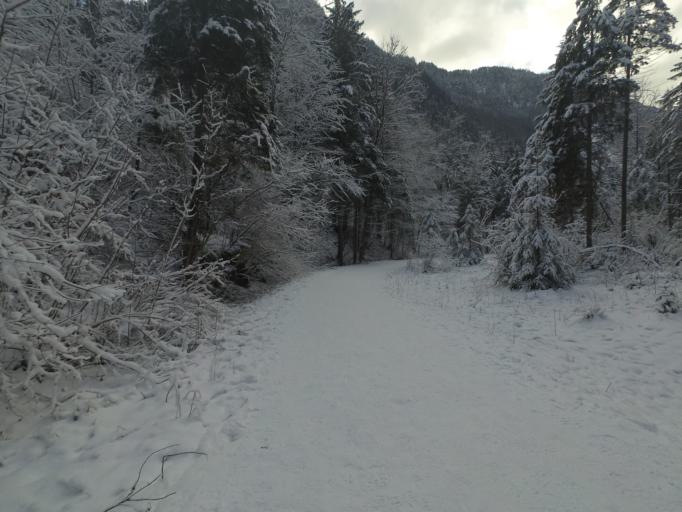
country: AT
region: Salzburg
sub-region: Politischer Bezirk Hallein
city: Golling an der Salzach
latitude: 47.5793
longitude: 13.1437
